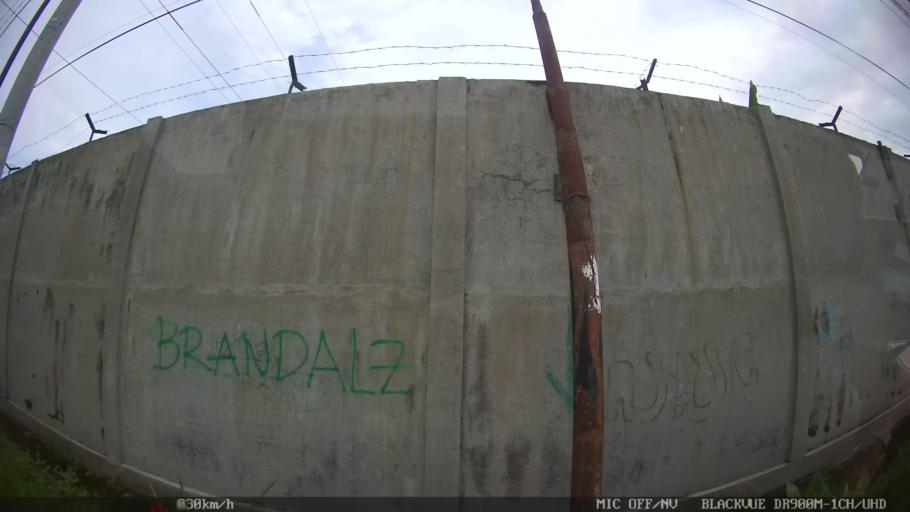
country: ID
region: North Sumatra
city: Sunggal
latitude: 3.6145
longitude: 98.5888
